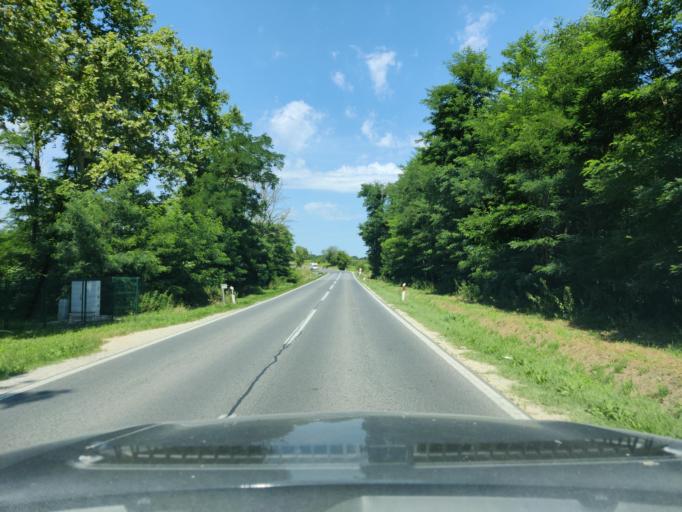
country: HR
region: Medimurska
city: Mackovec
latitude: 46.4568
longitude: 16.4306
